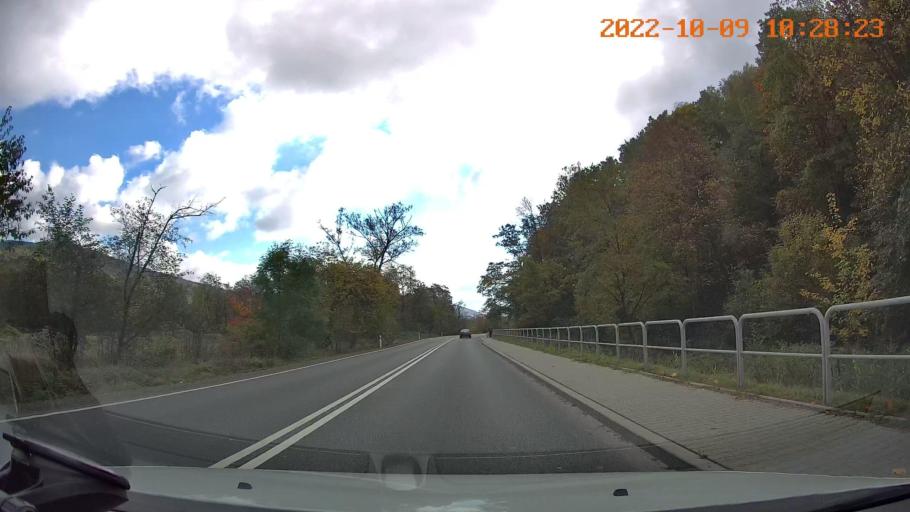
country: PL
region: Lesser Poland Voivodeship
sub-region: Powiat myslenicki
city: Lubien
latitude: 49.7185
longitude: 19.9868
